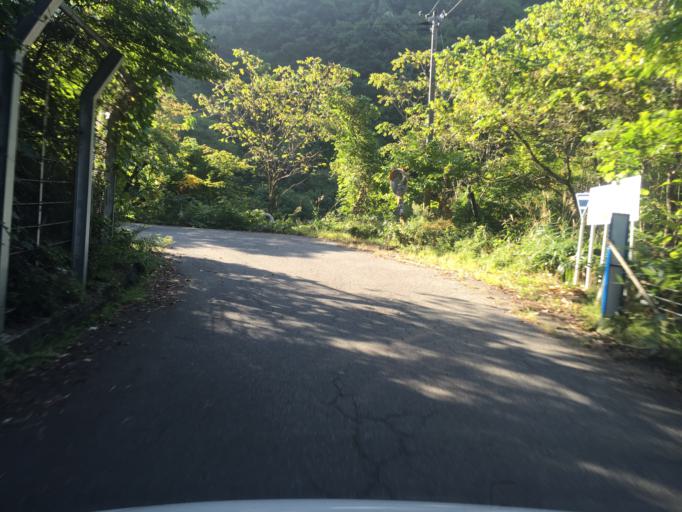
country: JP
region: Fukushima
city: Inawashiro
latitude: 37.4282
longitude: 139.9828
